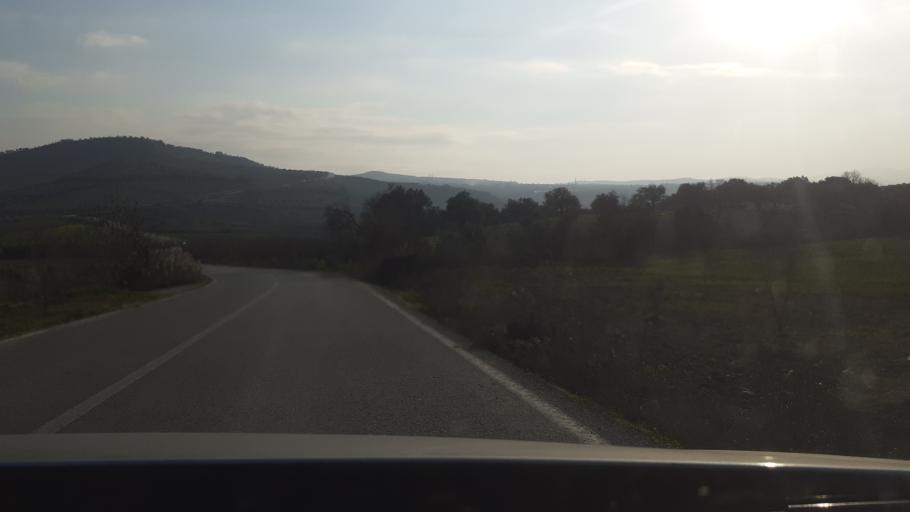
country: TR
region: Hatay
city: Oymakli
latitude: 36.1302
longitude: 36.3101
